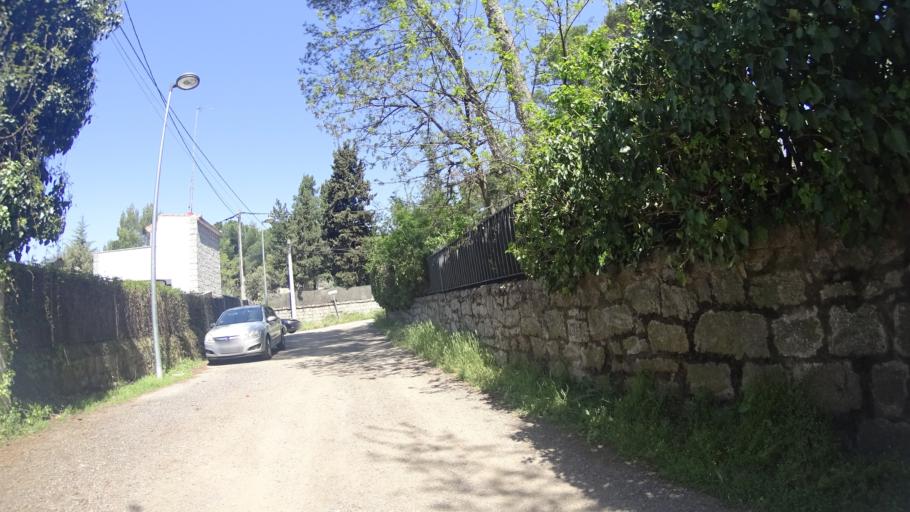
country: ES
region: Madrid
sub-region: Provincia de Madrid
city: Torrelodones
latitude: 40.5856
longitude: -3.9640
